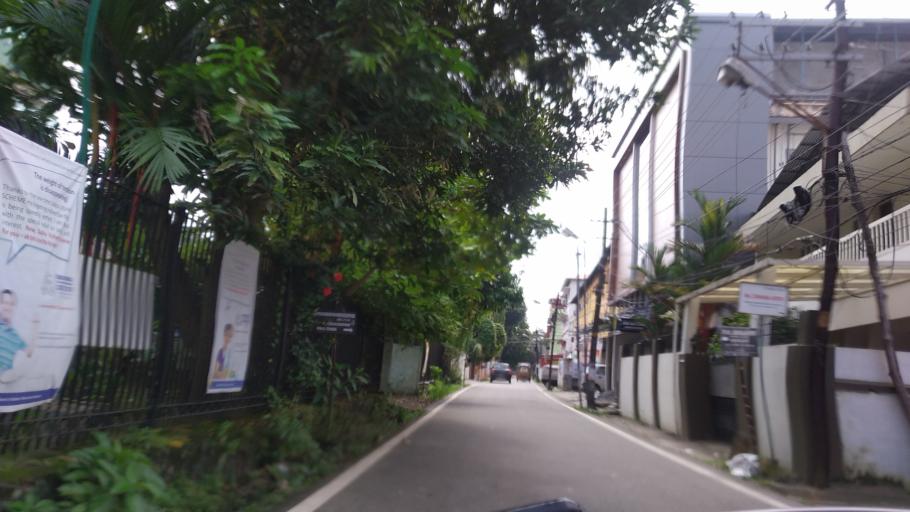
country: IN
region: Kerala
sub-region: Ernakulam
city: Cochin
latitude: 9.9871
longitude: 76.2794
